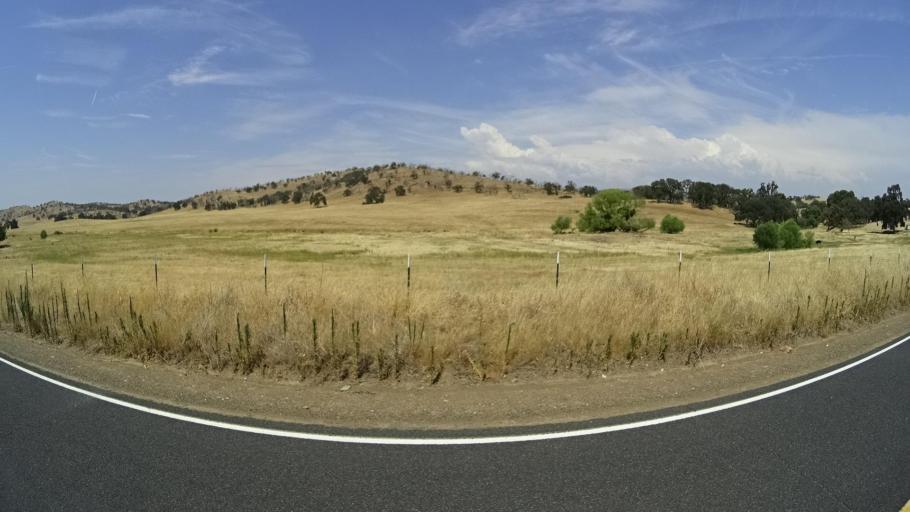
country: US
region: California
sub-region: Merced County
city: Planada
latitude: 37.4903
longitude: -120.2215
